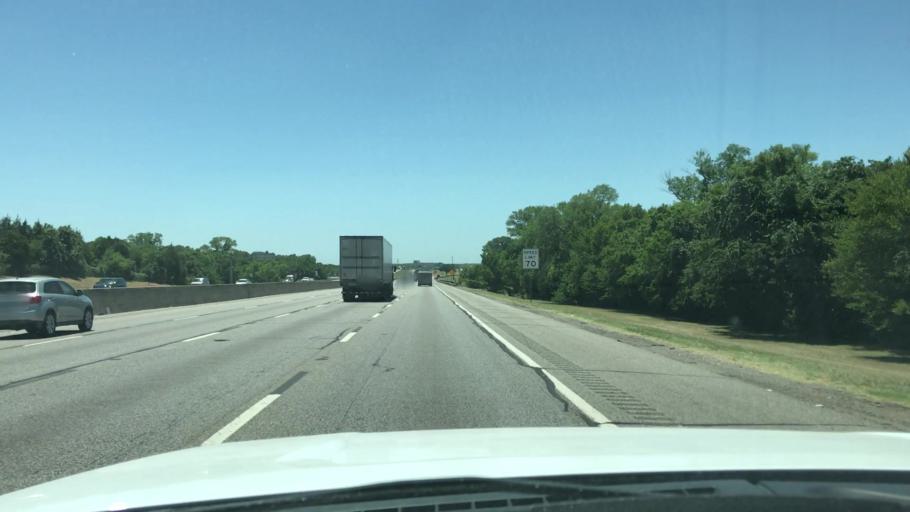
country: US
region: Texas
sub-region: Dallas County
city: Hutchins
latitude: 32.6811
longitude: -96.6668
